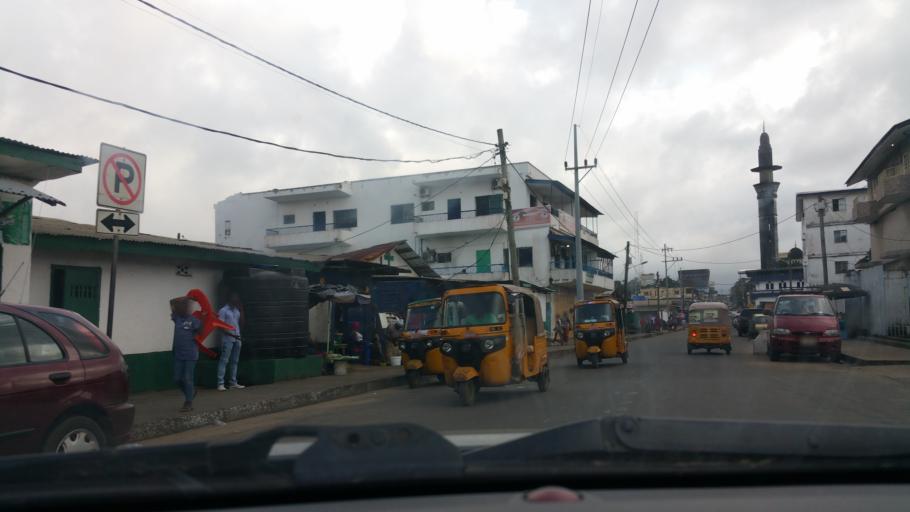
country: LR
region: Montserrado
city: Monrovia
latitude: 6.3116
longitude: -10.8110
